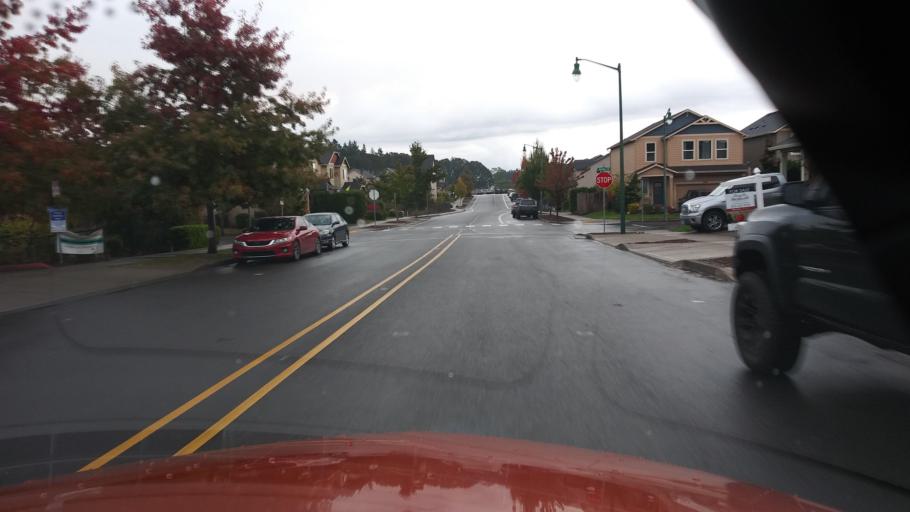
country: US
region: Oregon
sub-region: Washington County
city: Forest Grove
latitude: 45.5274
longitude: -123.0965
